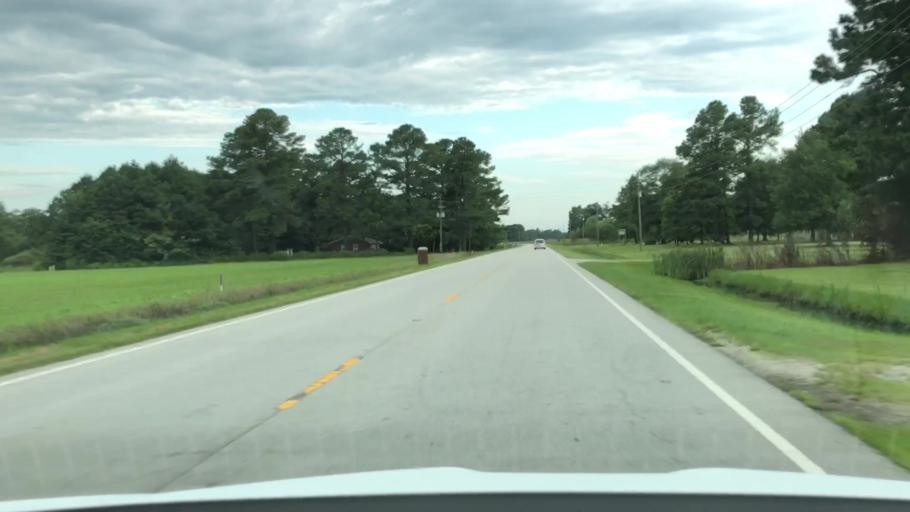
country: US
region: North Carolina
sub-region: Jones County
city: Trenton
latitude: 35.0762
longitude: -77.3918
